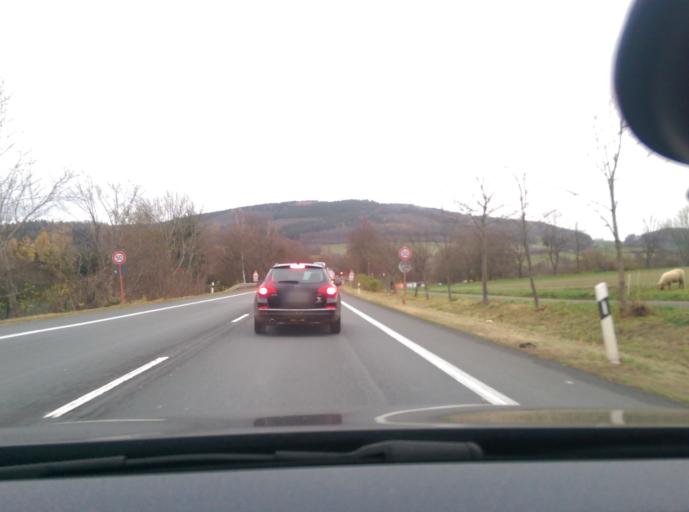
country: DE
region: Hesse
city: Witzenhausen
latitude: 51.3425
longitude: 9.8876
